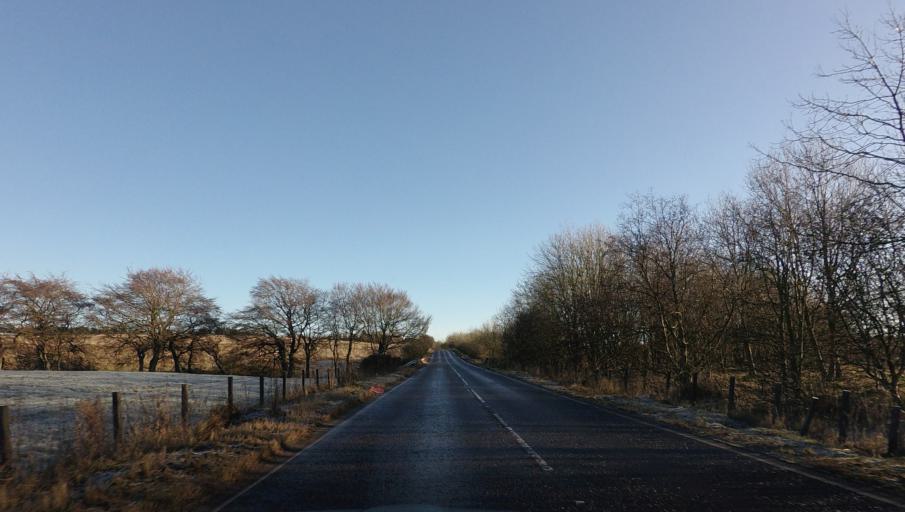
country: GB
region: Scotland
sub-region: North Lanarkshire
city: Shotts
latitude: 55.8083
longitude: -3.7916
